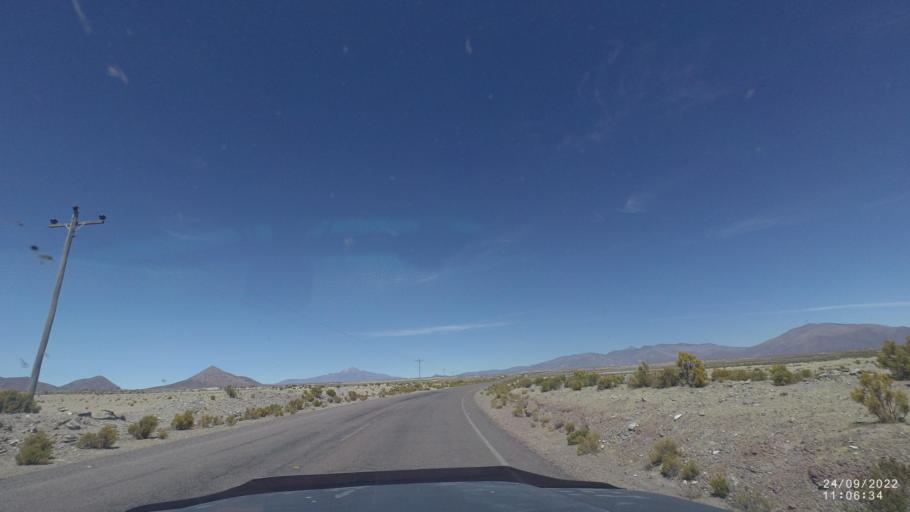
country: BO
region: Oruro
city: Challapata
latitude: -19.4766
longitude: -67.4313
